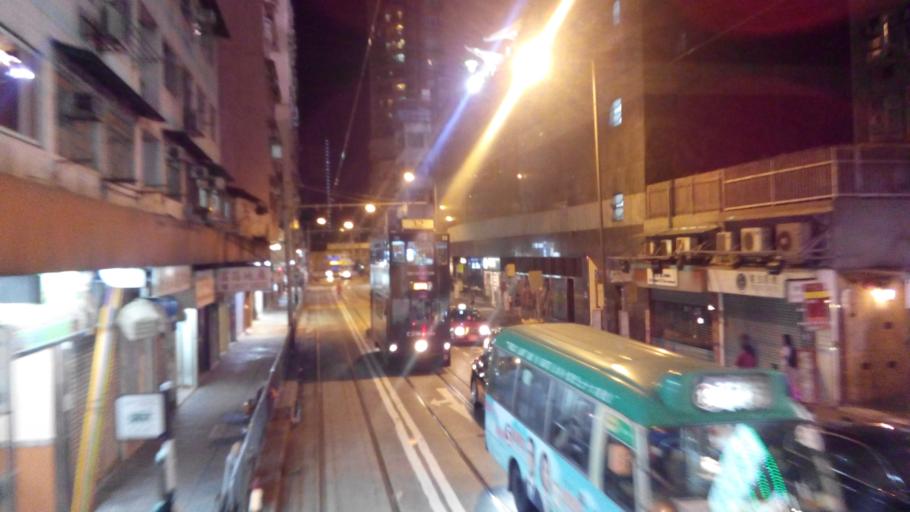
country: HK
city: Hong Kong
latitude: 22.2830
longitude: 114.1281
